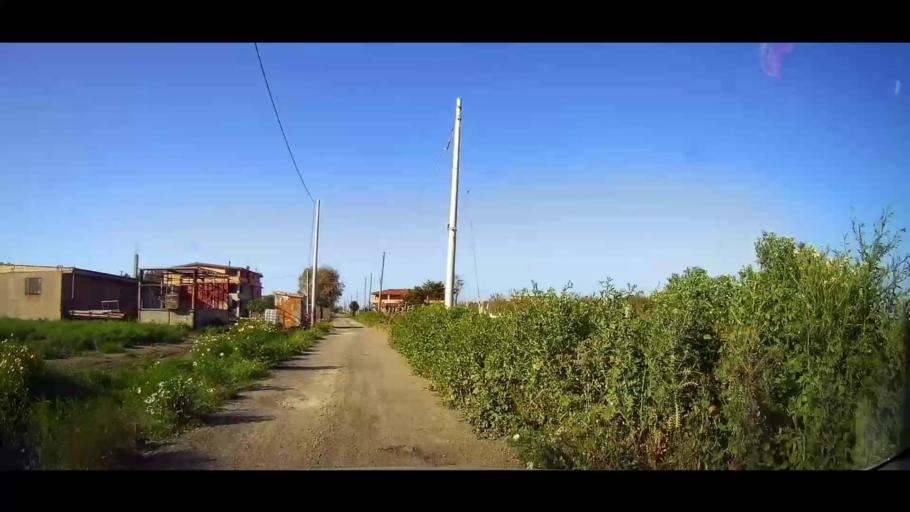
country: IT
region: Calabria
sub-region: Provincia di Crotone
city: Crotone
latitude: 39.0215
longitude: 17.1865
